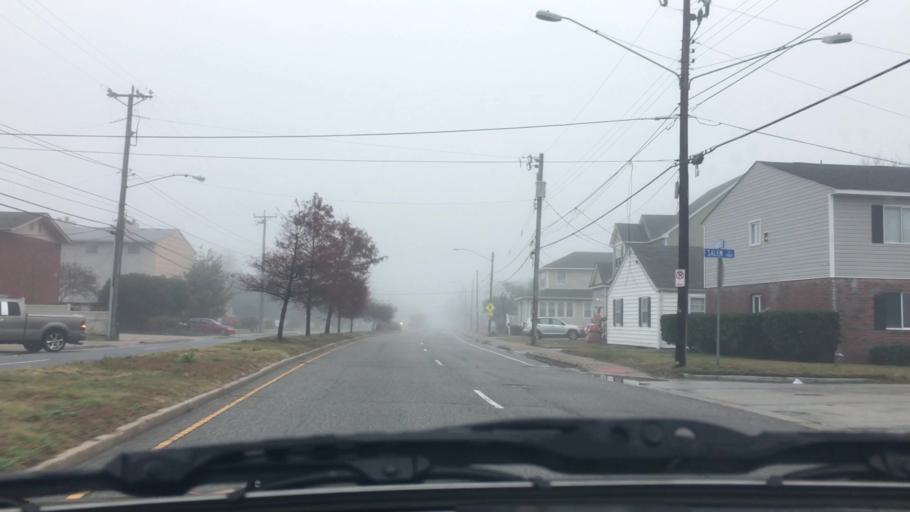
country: US
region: Virginia
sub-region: City of Hampton
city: East Hampton
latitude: 36.9666
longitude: -76.2767
